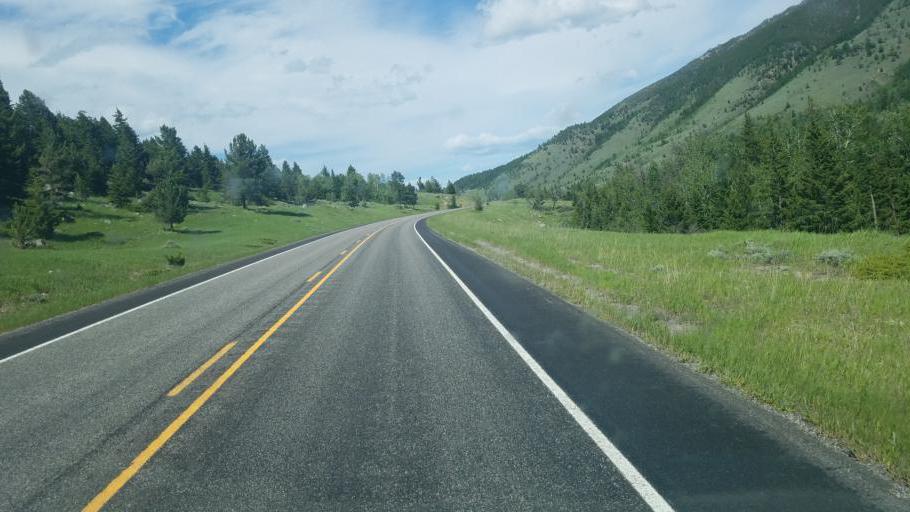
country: US
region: Montana
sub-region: Carbon County
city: Red Lodge
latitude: 45.0993
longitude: -109.3137
